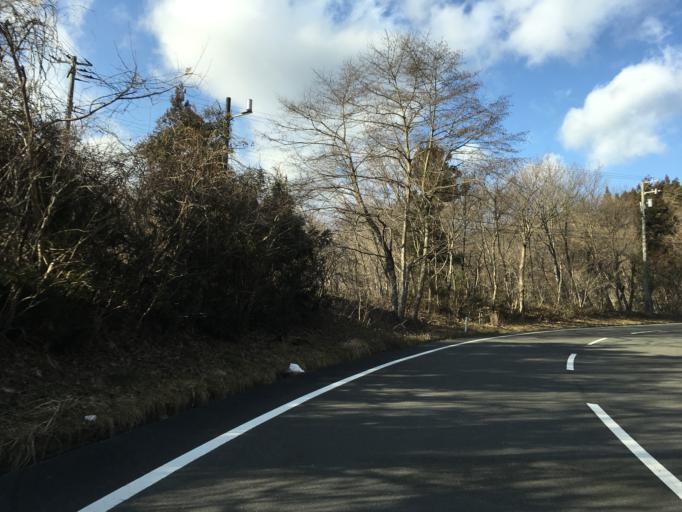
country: JP
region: Miyagi
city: Furukawa
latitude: 38.8087
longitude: 140.8254
